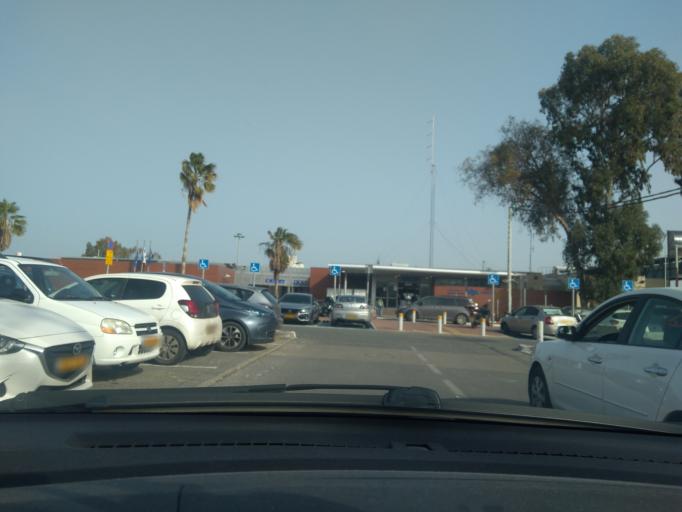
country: IL
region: Central District
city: Netanya
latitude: 32.3201
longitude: 34.8685
